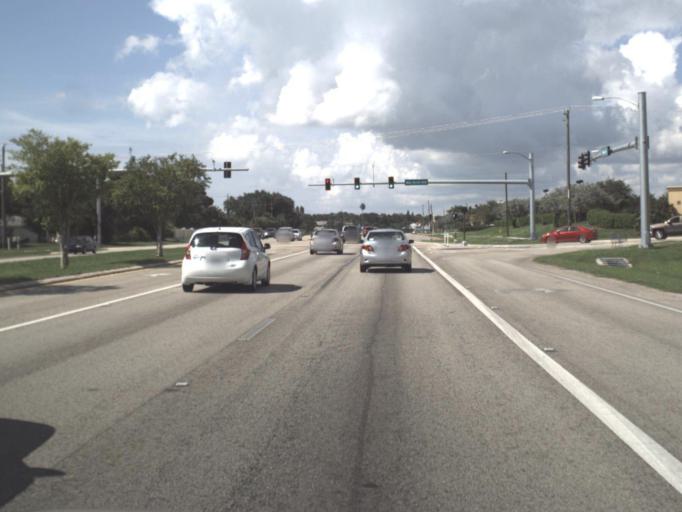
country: US
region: Florida
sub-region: Sarasota County
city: Osprey
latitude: 27.1911
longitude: -82.4880
